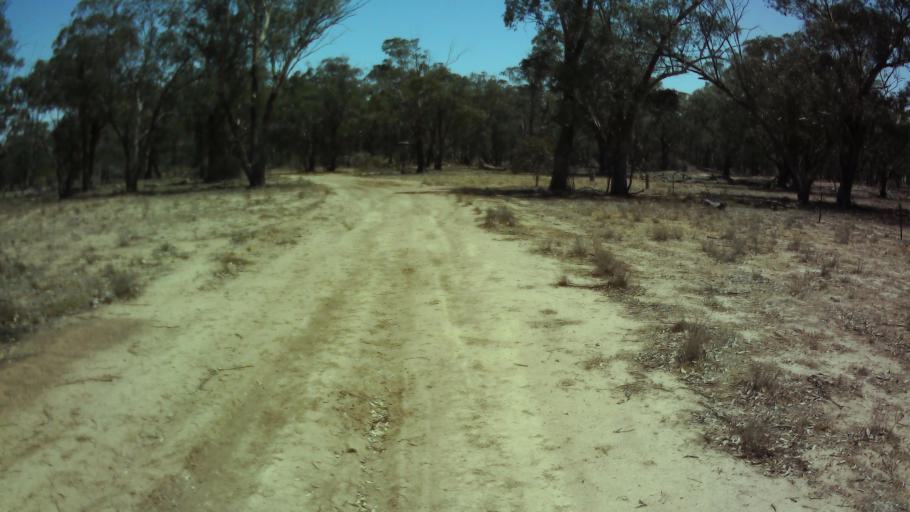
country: AU
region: New South Wales
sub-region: Weddin
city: Grenfell
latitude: -34.0704
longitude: 147.7908
